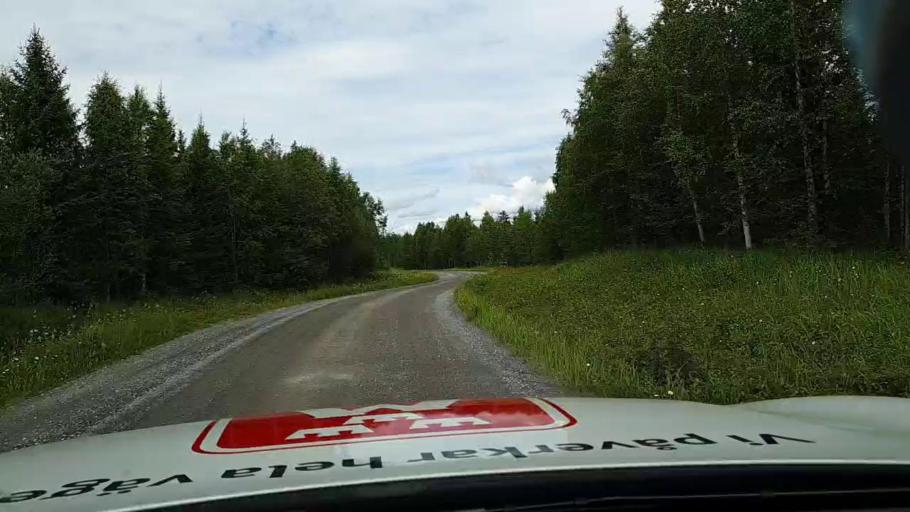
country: SE
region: Jaemtland
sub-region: OEstersunds Kommun
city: Lit
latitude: 63.3044
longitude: 15.2469
